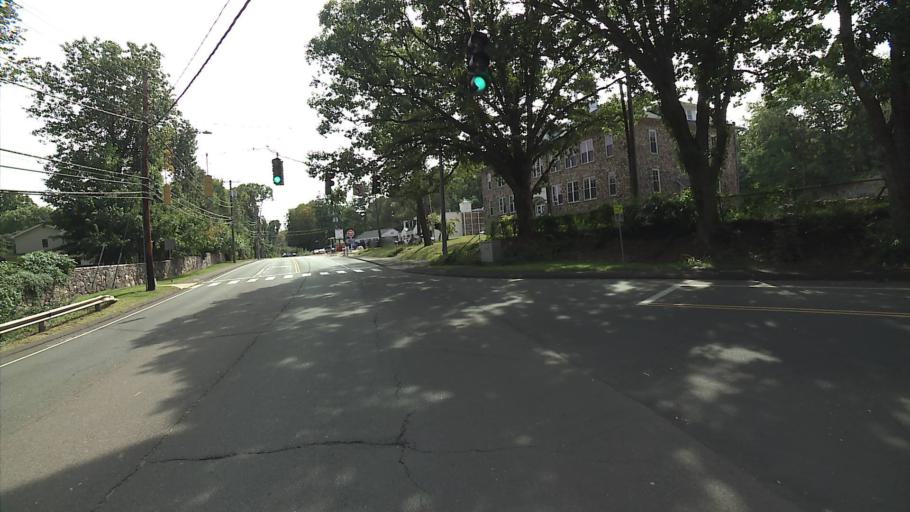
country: US
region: Connecticut
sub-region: Fairfield County
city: North Stamford
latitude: 41.1229
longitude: -73.5446
